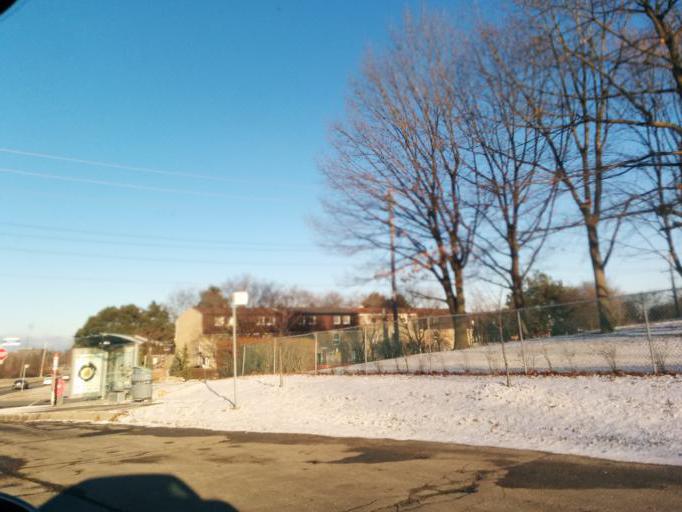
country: CA
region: Ontario
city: Etobicoke
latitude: 43.6451
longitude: -79.5904
